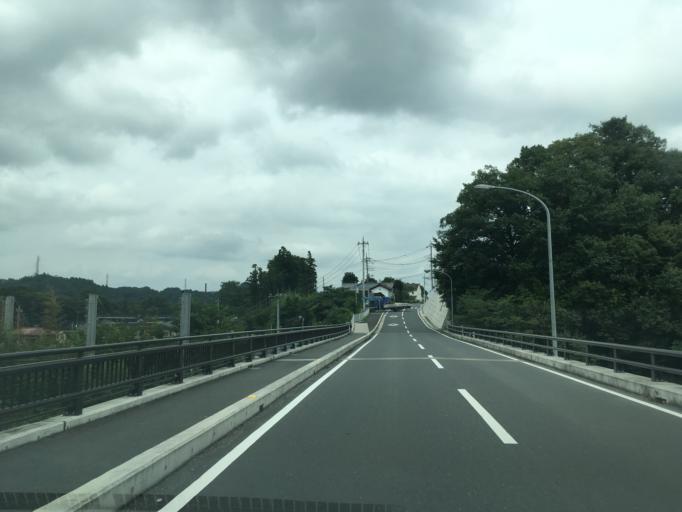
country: JP
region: Saitama
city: Chichibu
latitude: 35.9907
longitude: 139.1038
